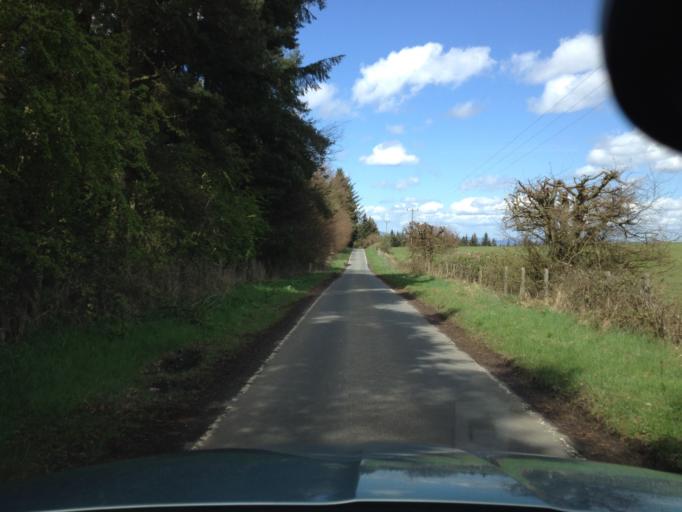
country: GB
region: Scotland
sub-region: West Lothian
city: Linlithgow
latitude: 55.9442
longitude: -3.5879
